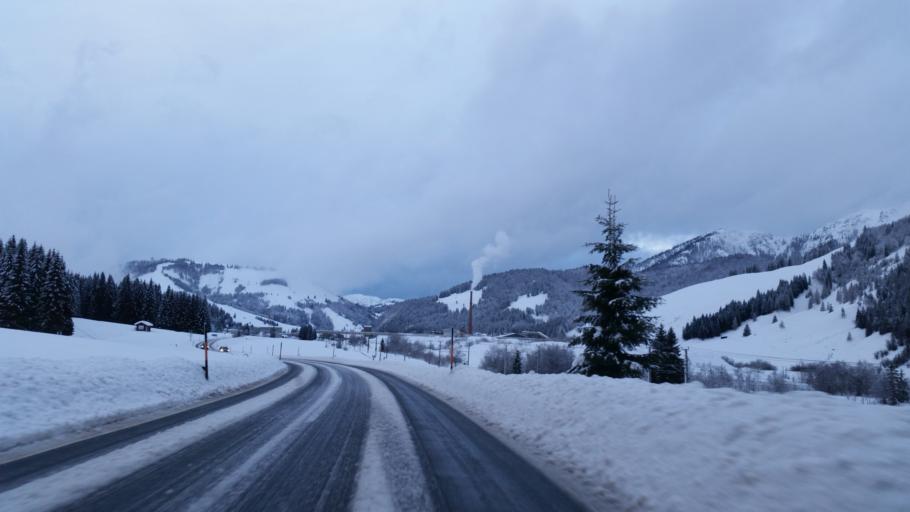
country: AT
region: Tyrol
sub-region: Politischer Bezirk Kitzbuhel
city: Hochfilzen
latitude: 47.4570
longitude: 12.6427
